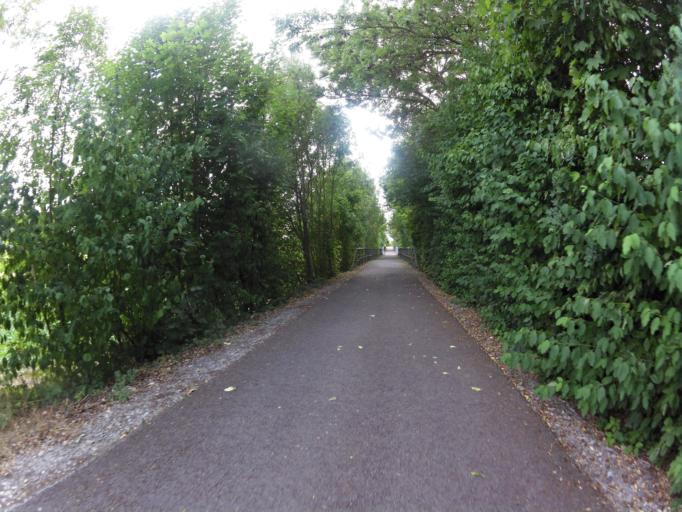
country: DE
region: Bavaria
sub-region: Regierungsbezirk Unterfranken
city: Sonderhofen
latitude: 49.5937
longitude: 10.0063
